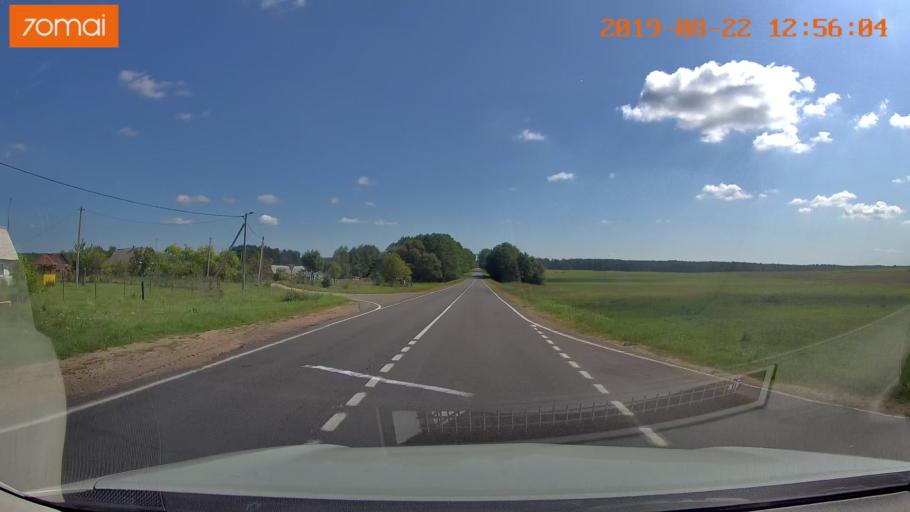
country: BY
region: Minsk
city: Prawdzinski
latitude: 53.4344
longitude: 27.7244
